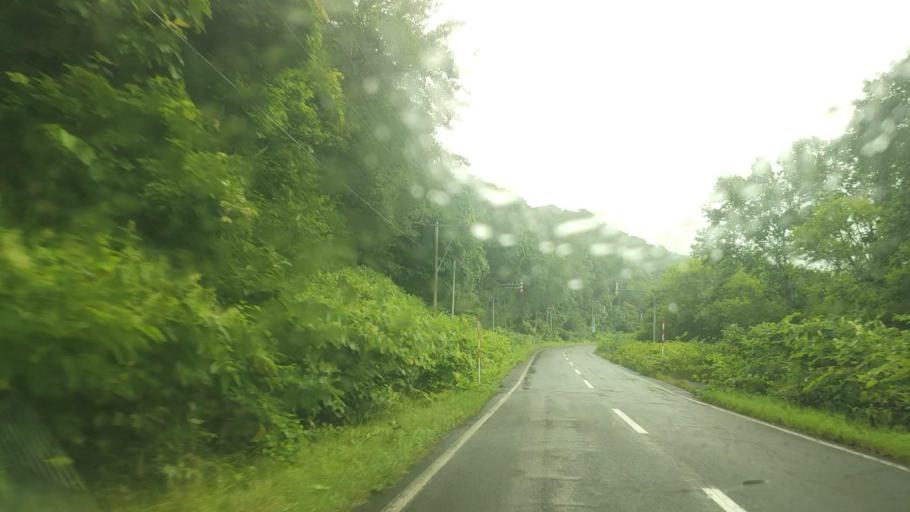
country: JP
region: Hokkaido
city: Date
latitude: 42.5421
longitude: 141.0165
